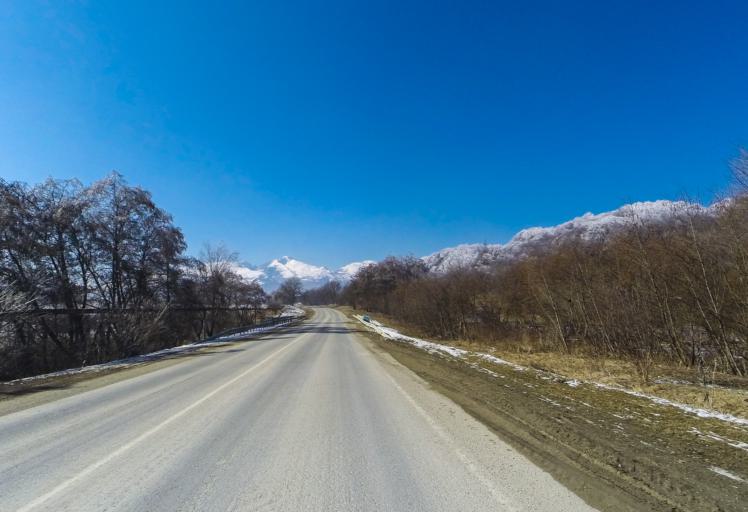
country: RU
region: Kabardino-Balkariya
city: Babugent
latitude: 43.2971
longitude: 43.5784
